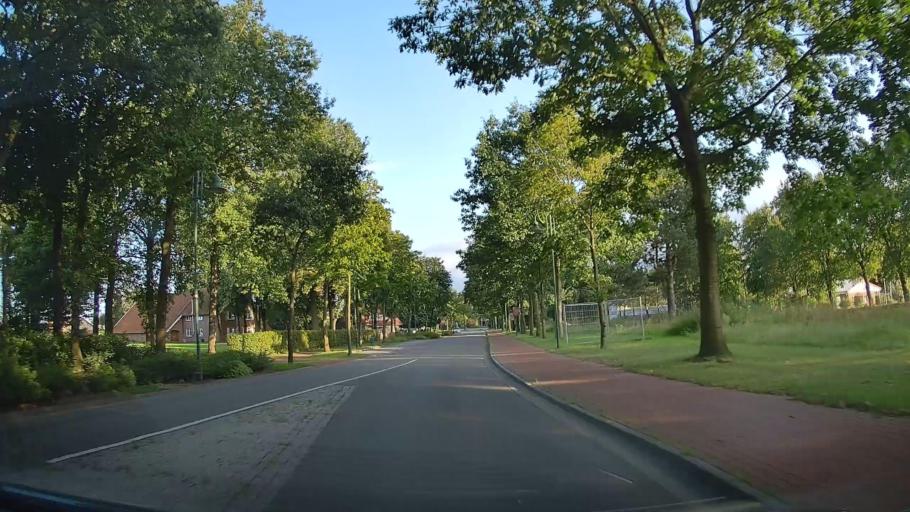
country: DE
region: Lower Saxony
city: Hilkenbrook
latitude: 53.0378
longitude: 7.7436
